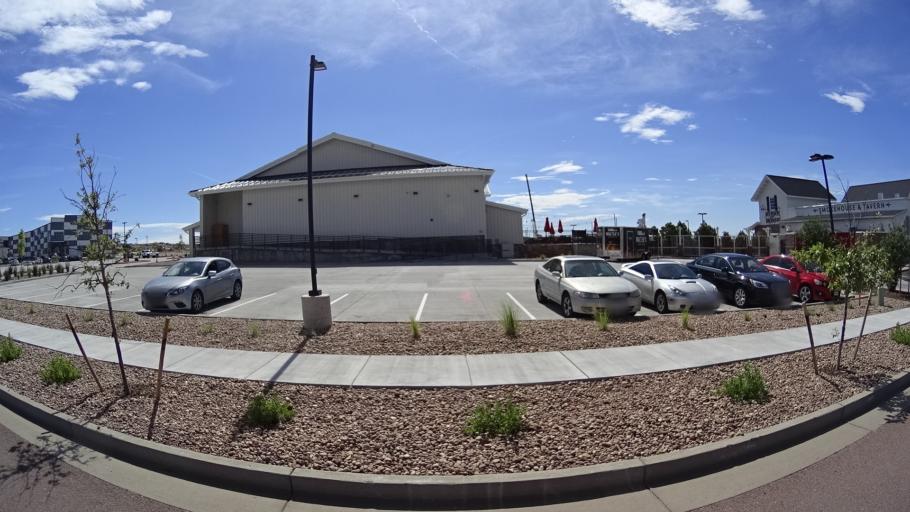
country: US
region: Colorado
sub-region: El Paso County
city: Gleneagle
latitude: 39.0231
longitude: -104.8251
